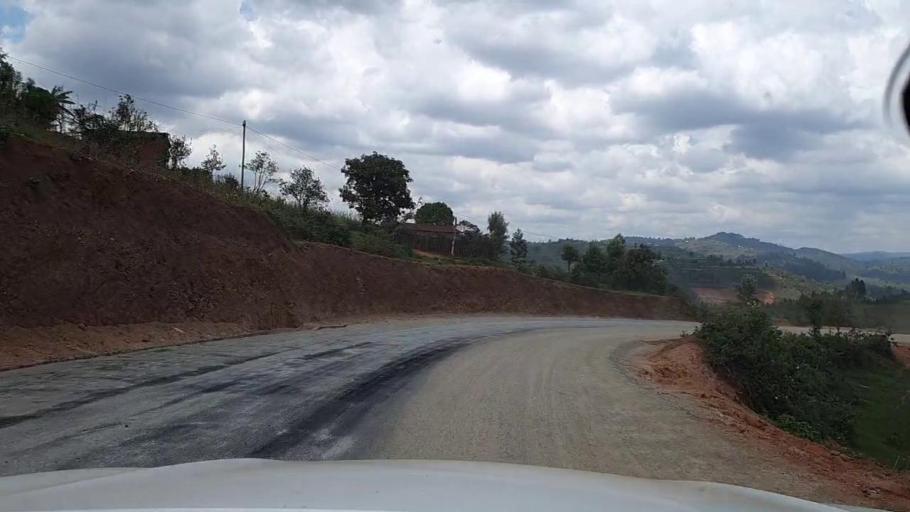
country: RW
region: Southern Province
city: Butare
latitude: -2.6984
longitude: 29.5635
